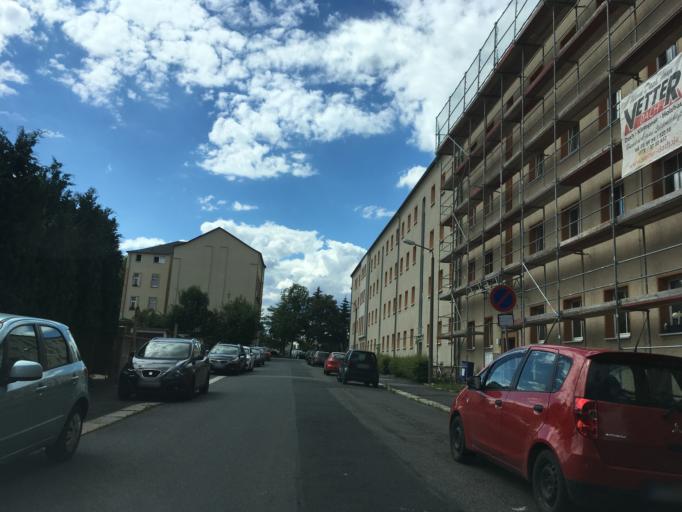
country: DE
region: Saxony
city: Radeberg
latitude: 51.1116
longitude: 13.9199
